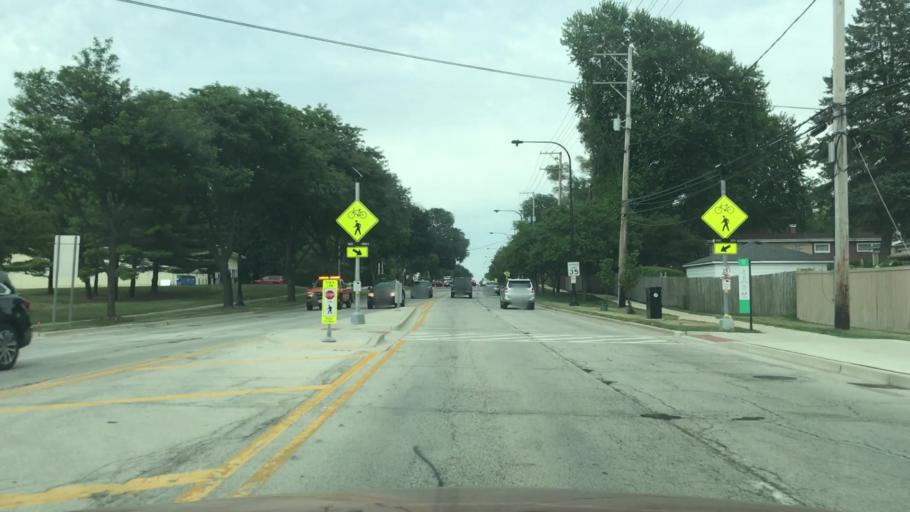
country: US
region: Illinois
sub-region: Cook County
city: Mount Prospect
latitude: 42.0664
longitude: -87.9577
